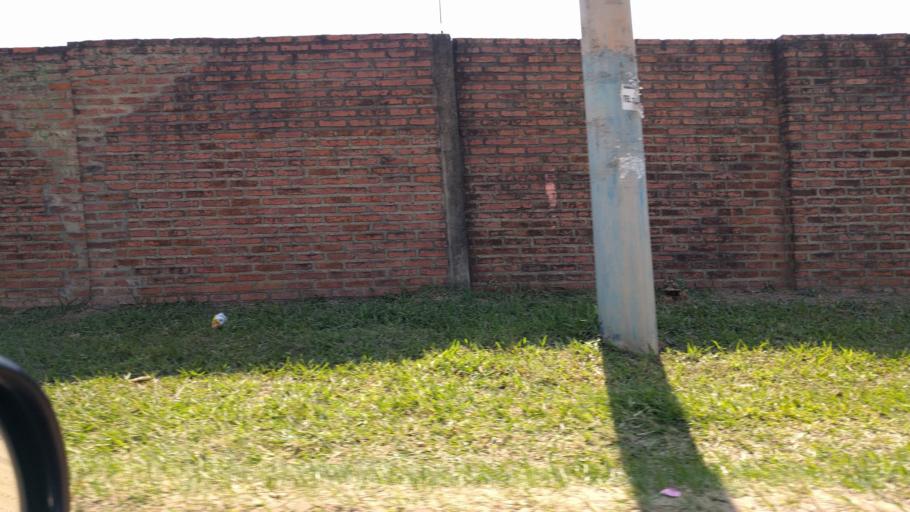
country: BO
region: Santa Cruz
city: Santa Cruz de la Sierra
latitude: -17.7537
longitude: -63.2201
